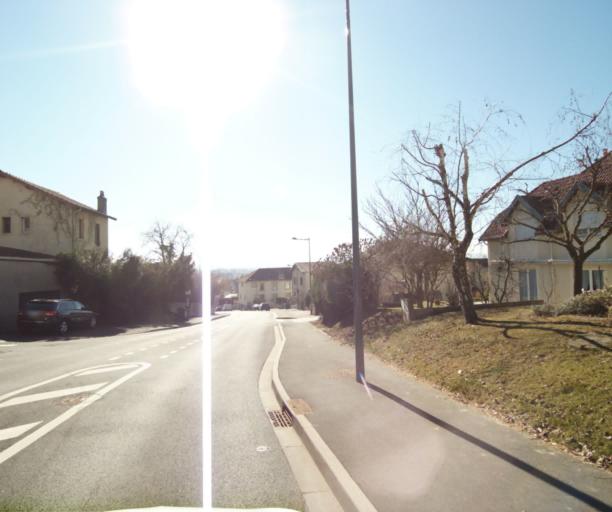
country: FR
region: Lorraine
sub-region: Departement de Meurthe-et-Moselle
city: Essey-les-Nancy
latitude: 48.7080
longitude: 6.2194
